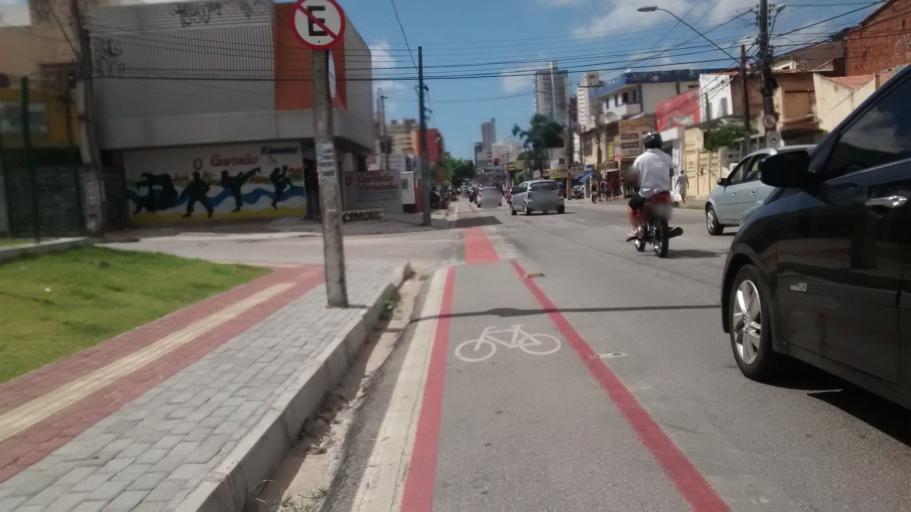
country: BR
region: Ceara
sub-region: Fortaleza
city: Fortaleza
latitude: -3.7408
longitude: -38.5172
